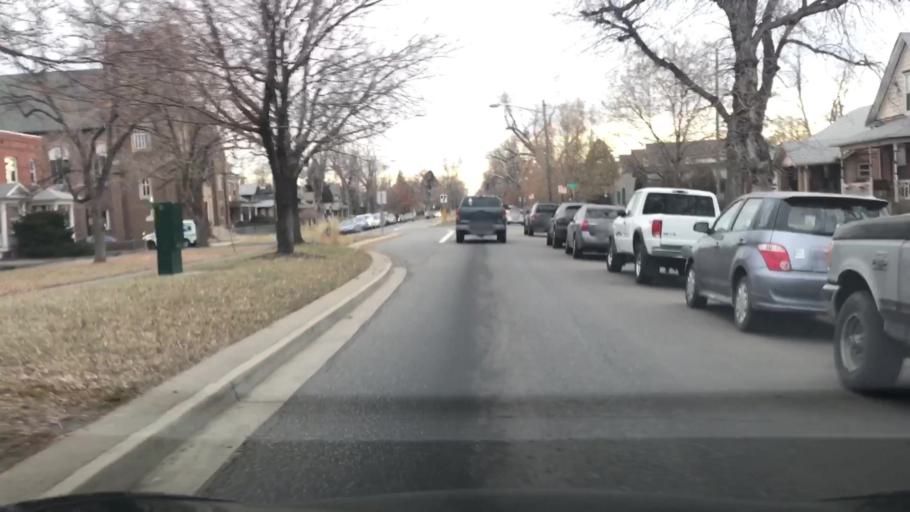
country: US
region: Colorado
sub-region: Denver County
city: Denver
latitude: 39.7099
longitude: -104.9829
